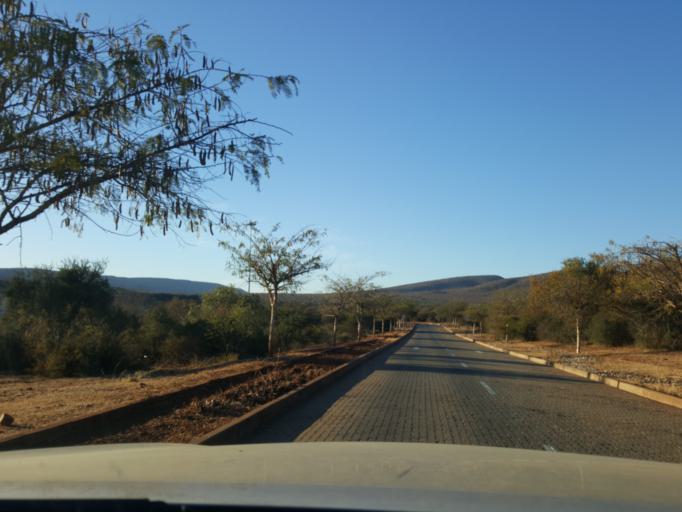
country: BW
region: South East
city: Lobatse
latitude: -25.2809
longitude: 25.7179
